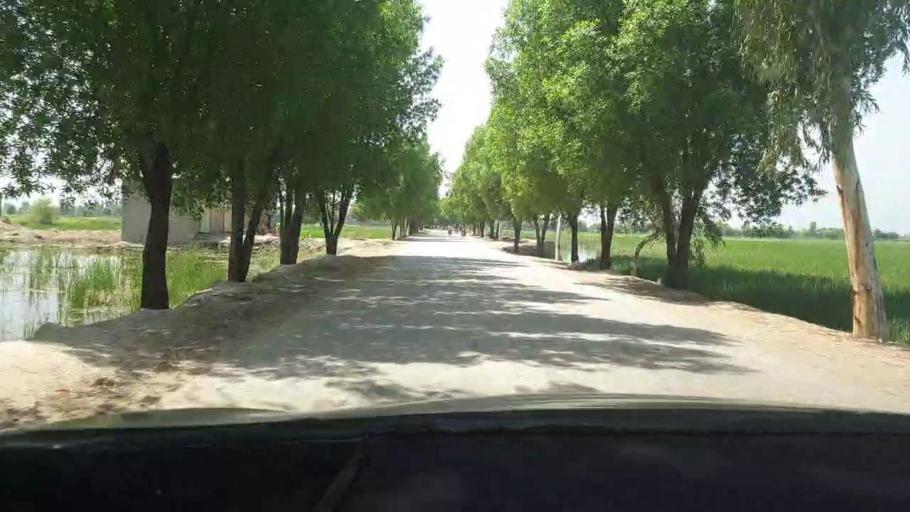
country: PK
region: Sindh
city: Miro Khan
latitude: 27.6718
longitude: 68.0561
